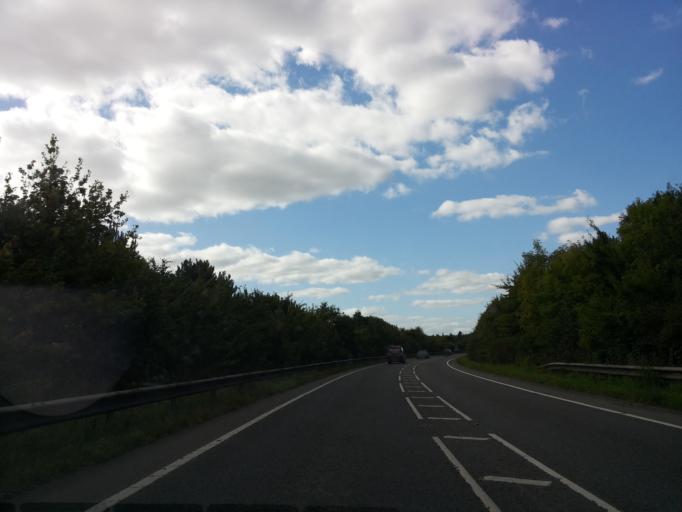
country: GB
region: England
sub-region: Wiltshire
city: Bishopstrow
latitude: 51.1828
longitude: -2.1298
